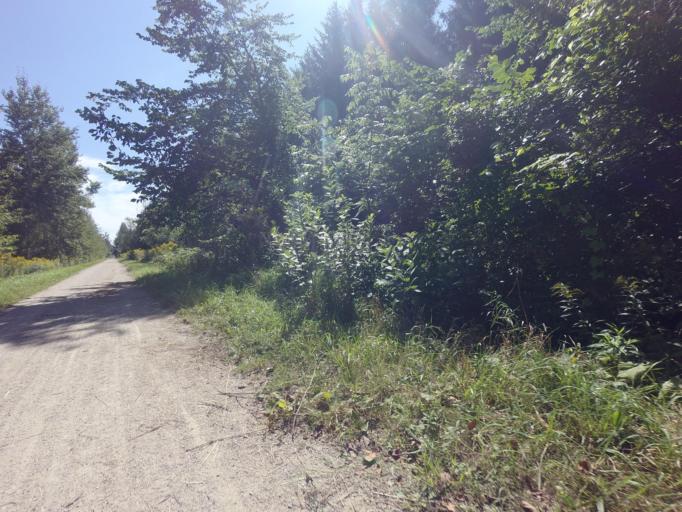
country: CA
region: Ontario
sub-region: Wellington County
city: Guelph
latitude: 43.7371
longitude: -80.3468
